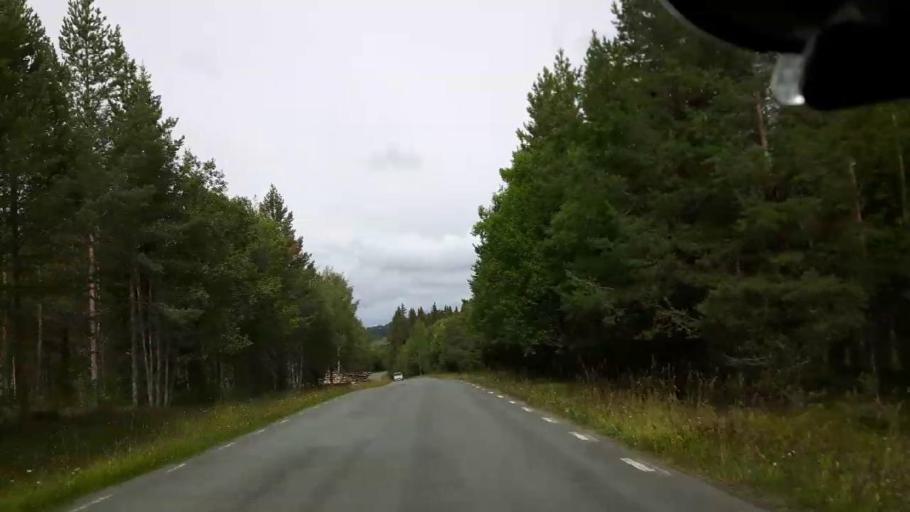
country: SE
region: Jaemtland
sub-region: Krokoms Kommun
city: Valla
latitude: 63.4692
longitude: 14.0106
